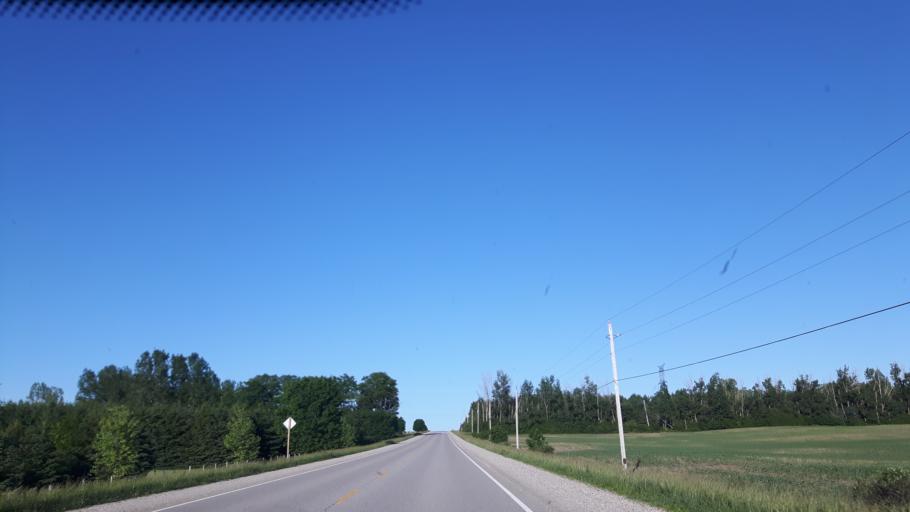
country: CA
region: Ontario
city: Goderich
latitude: 43.6426
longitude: -81.6403
